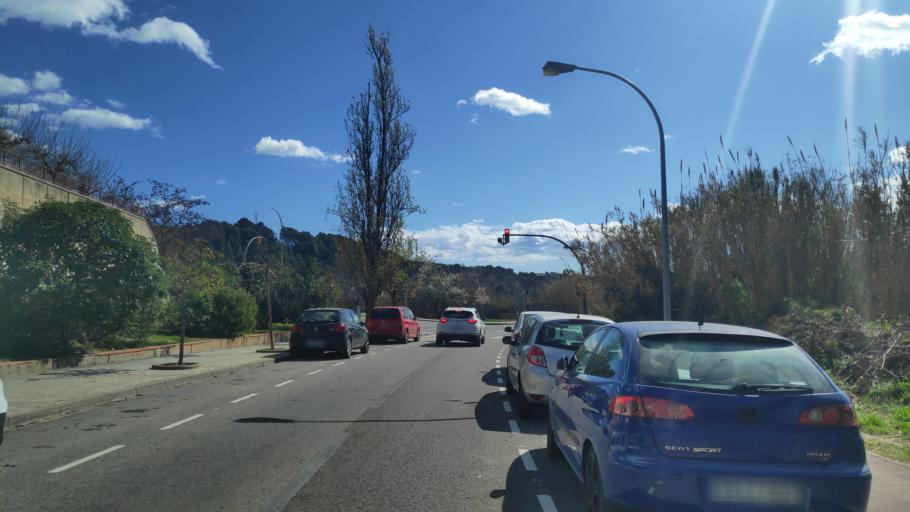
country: ES
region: Catalonia
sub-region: Provincia de Barcelona
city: Sabadell
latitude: 41.5479
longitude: 2.1228
